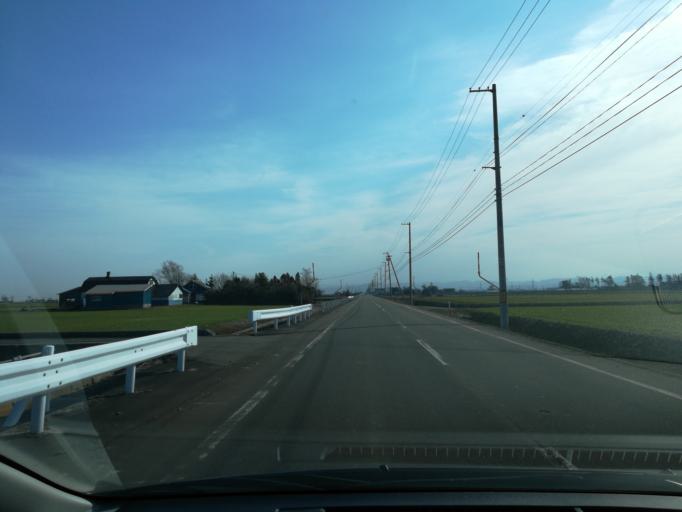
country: JP
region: Hokkaido
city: Iwamizawa
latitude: 43.1695
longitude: 141.6663
